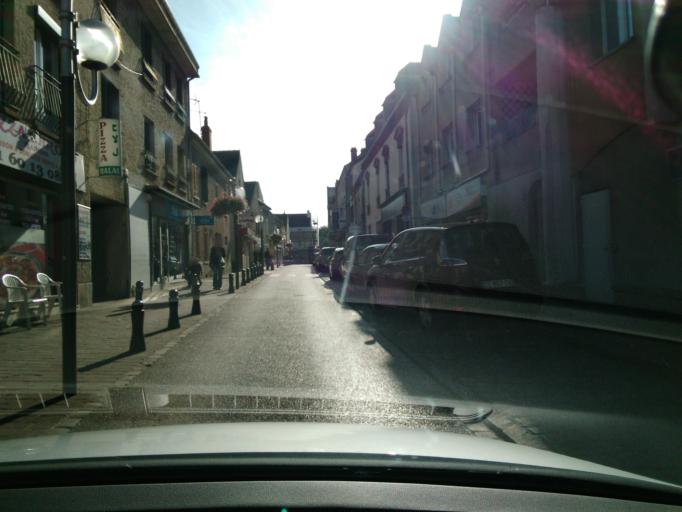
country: FR
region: Ile-de-France
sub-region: Departement de l'Essonne
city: Massy
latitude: 48.7301
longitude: 2.2744
